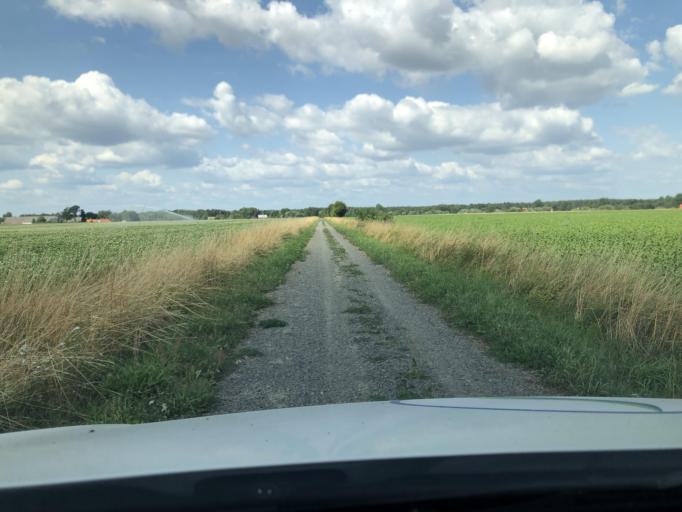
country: SE
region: Skane
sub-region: Kristianstads Kommun
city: Degeberga
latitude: 55.8897
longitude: 14.0806
